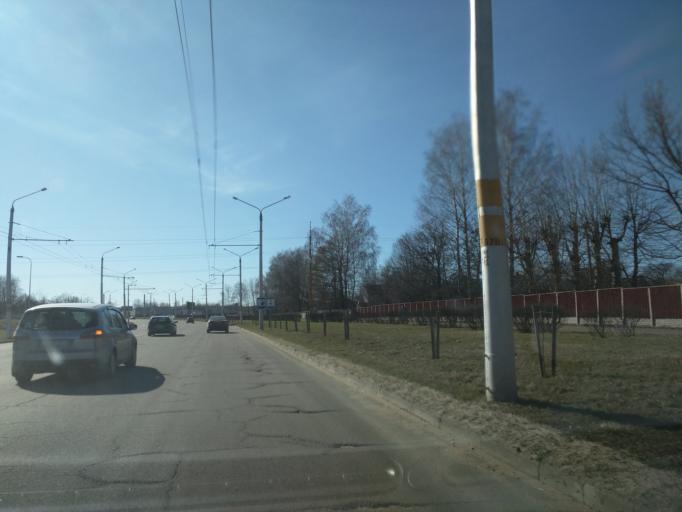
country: BY
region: Mogilev
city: Babruysk
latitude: 53.1845
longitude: 29.2197
